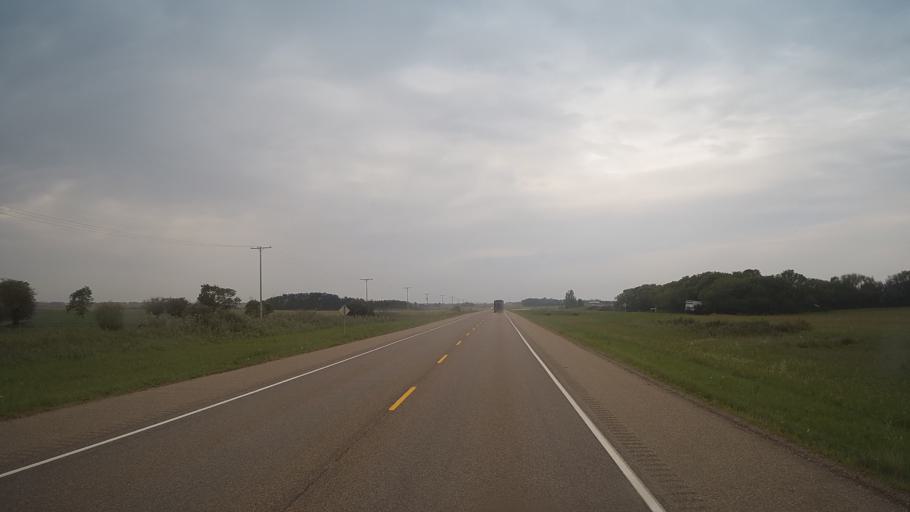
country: CA
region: Saskatchewan
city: Langham
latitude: 52.1289
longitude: -107.1168
